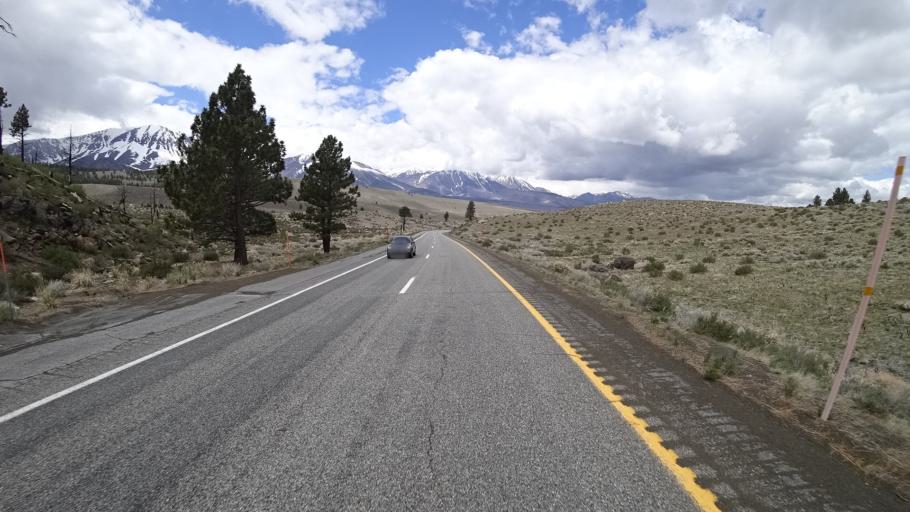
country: US
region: California
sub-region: Mono County
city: Mammoth Lakes
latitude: 37.8289
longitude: -119.0682
